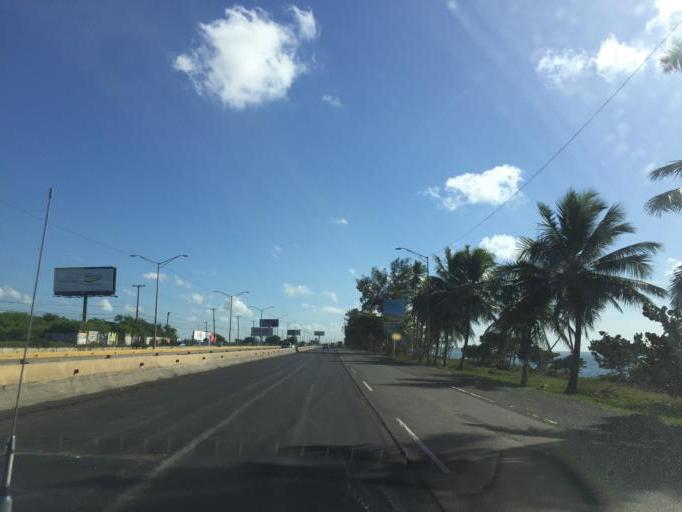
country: DO
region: Santo Domingo
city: Guerra
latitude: 18.4636
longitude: -69.7510
